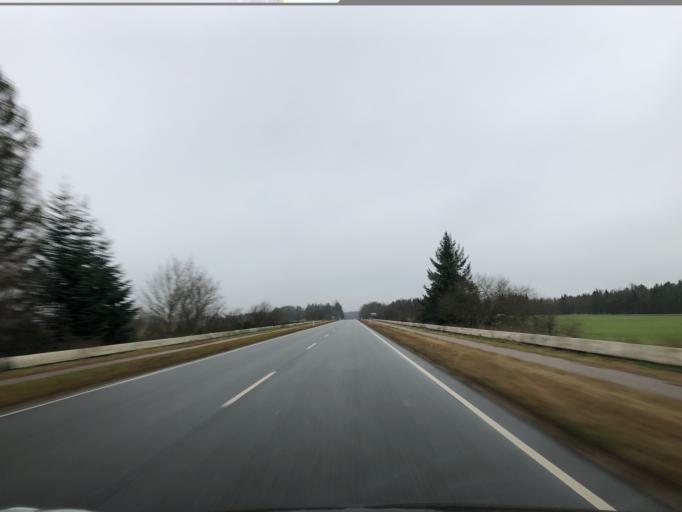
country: DK
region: Central Jutland
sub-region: Herning Kommune
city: Lind
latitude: 56.0725
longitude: 8.9879
